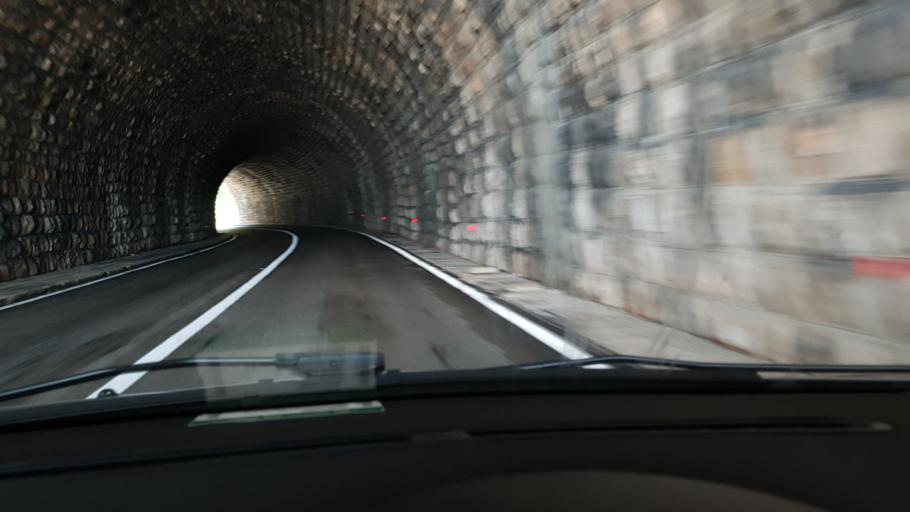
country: HR
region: Licko-Senjska
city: Senj
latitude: 44.8578
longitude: 14.9081
